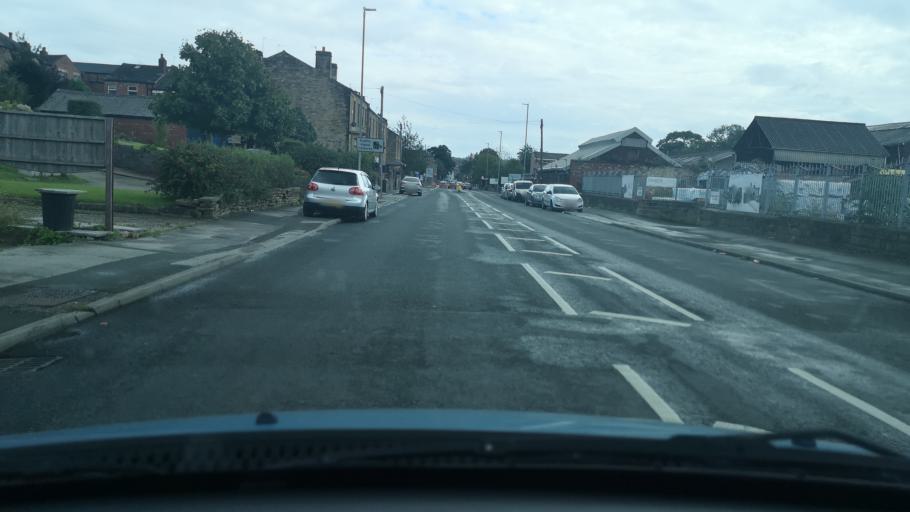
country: GB
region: England
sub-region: Kirklees
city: Batley
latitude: 53.7181
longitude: -1.6380
